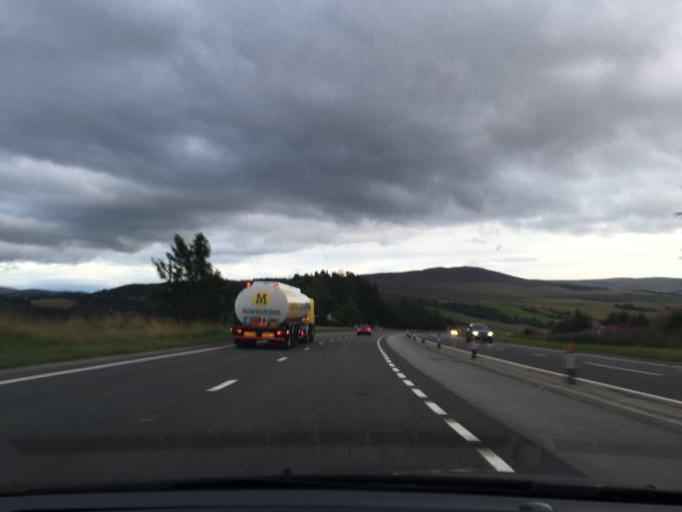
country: GB
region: Scotland
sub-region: Highland
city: Inverness
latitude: 57.4314
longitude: -4.1275
